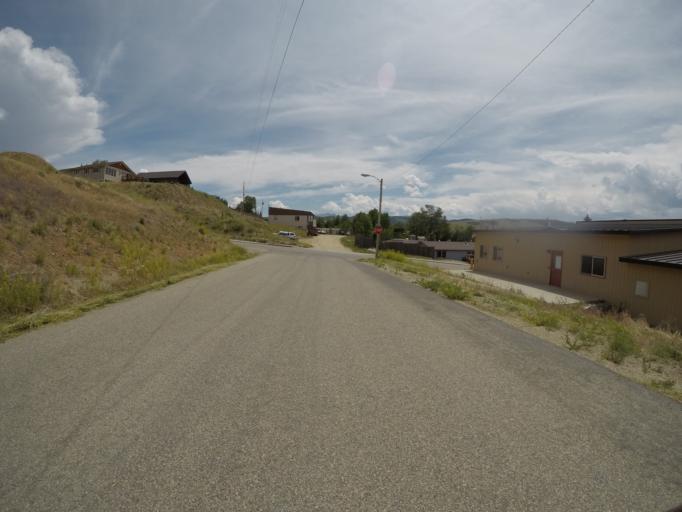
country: US
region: Colorado
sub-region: Grand County
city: Granby
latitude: 40.0858
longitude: -105.9326
